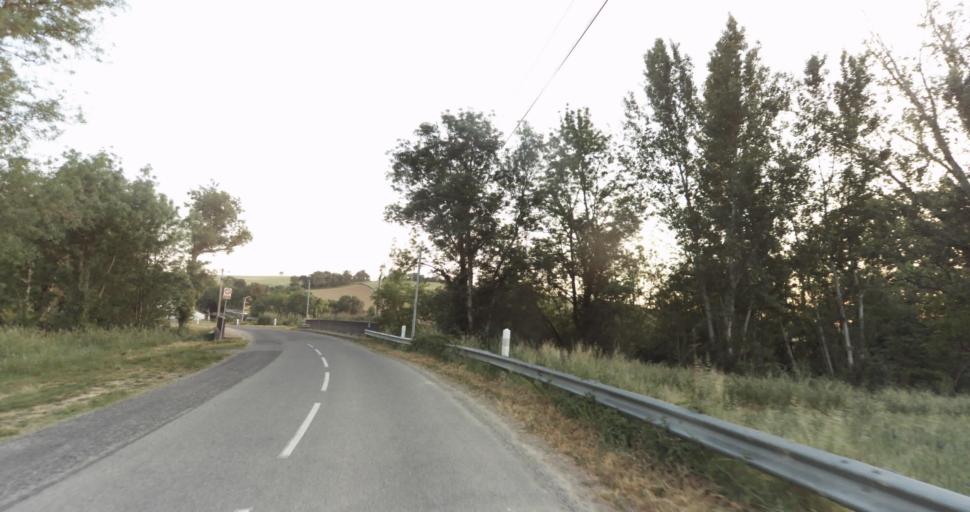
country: FR
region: Midi-Pyrenees
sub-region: Departement de la Haute-Garonne
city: Levignac
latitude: 43.6520
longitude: 1.1502
